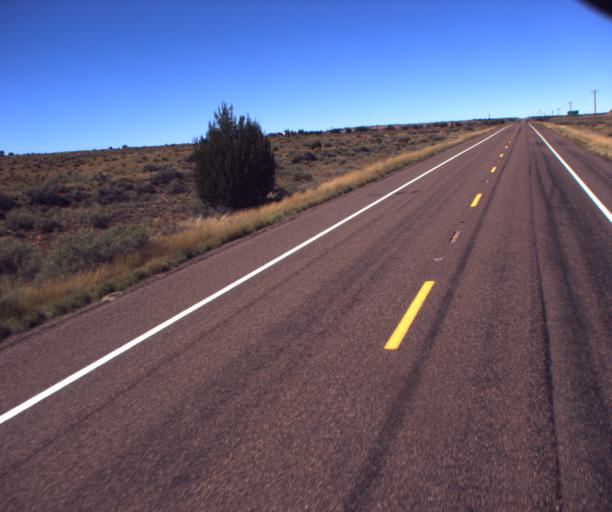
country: US
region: Arizona
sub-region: Apache County
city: Saint Johns
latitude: 34.6214
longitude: -109.6643
